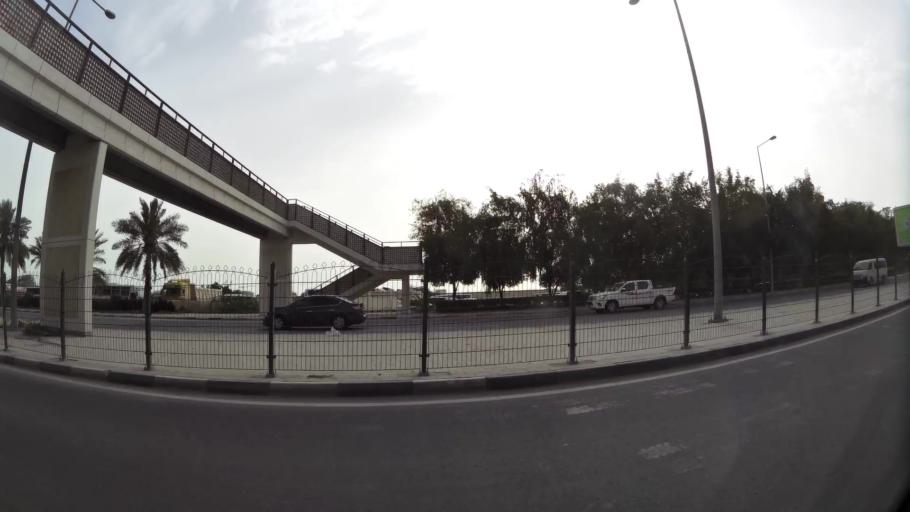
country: QA
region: Baladiyat ad Dawhah
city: Doha
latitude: 25.2756
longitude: 51.5524
